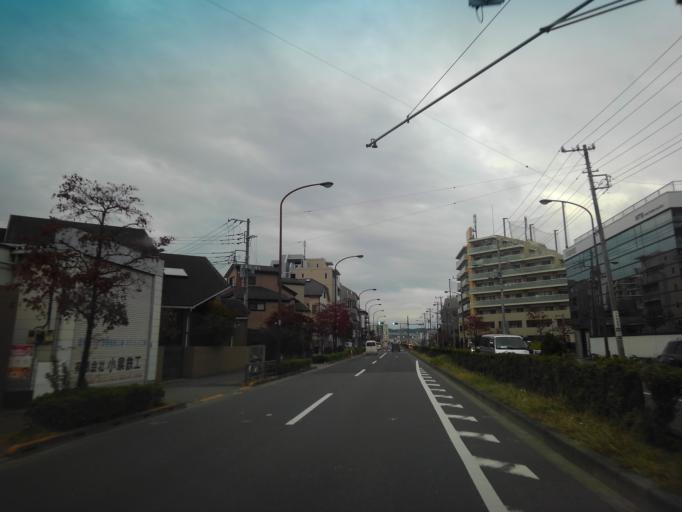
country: JP
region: Tokyo
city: Chofugaoka
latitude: 35.6473
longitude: 139.5307
